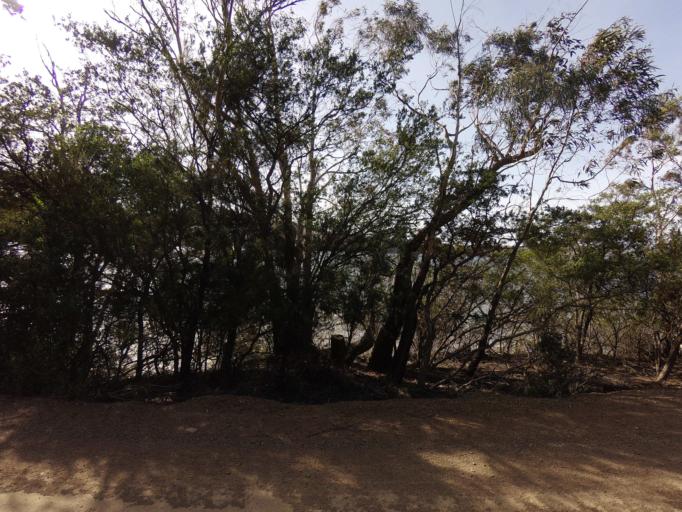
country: AU
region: Tasmania
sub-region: Kingborough
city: Kettering
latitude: -43.1143
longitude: 147.2706
